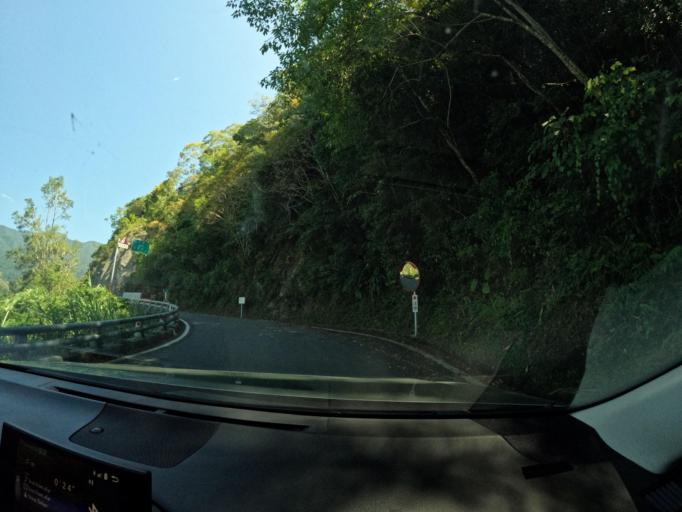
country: TW
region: Taiwan
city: Yujing
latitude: 23.2817
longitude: 120.8394
